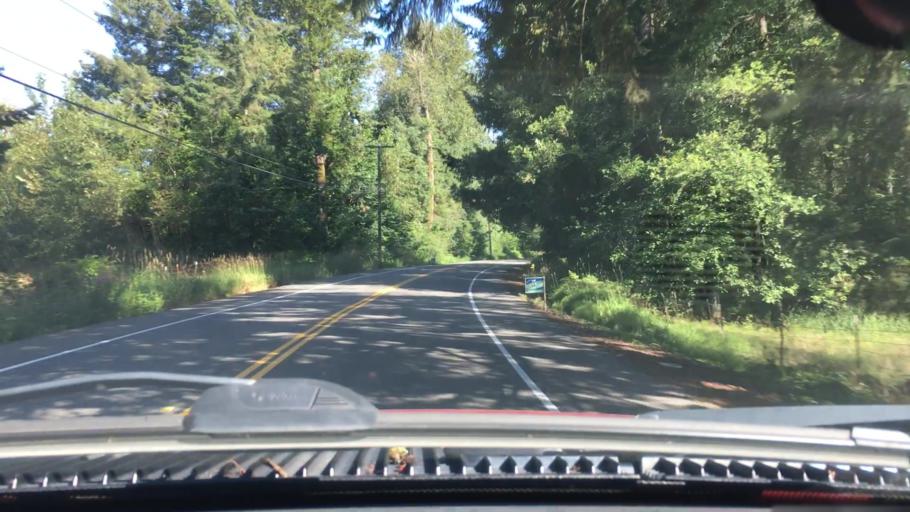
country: US
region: Washington
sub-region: King County
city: Lake Morton-Berrydale
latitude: 47.3319
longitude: -122.1210
